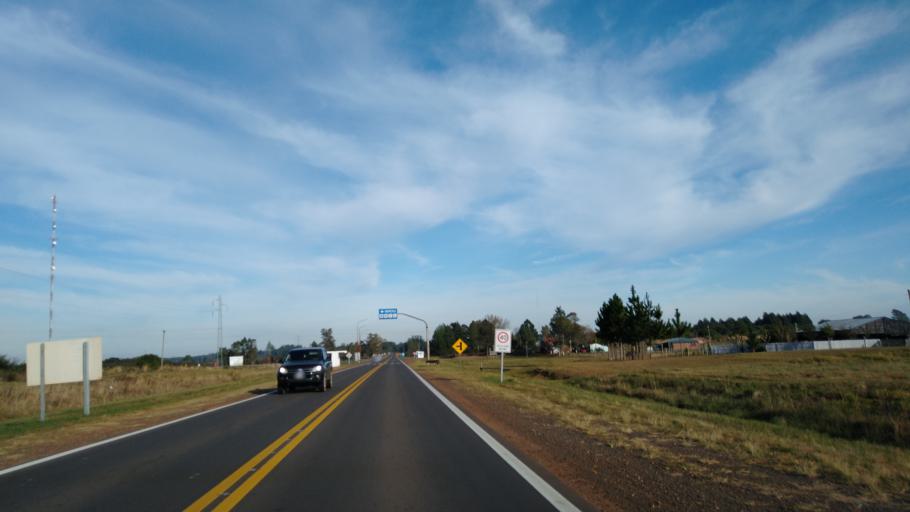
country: AR
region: Corrientes
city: Yapeyu
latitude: -29.4217
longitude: -56.8429
